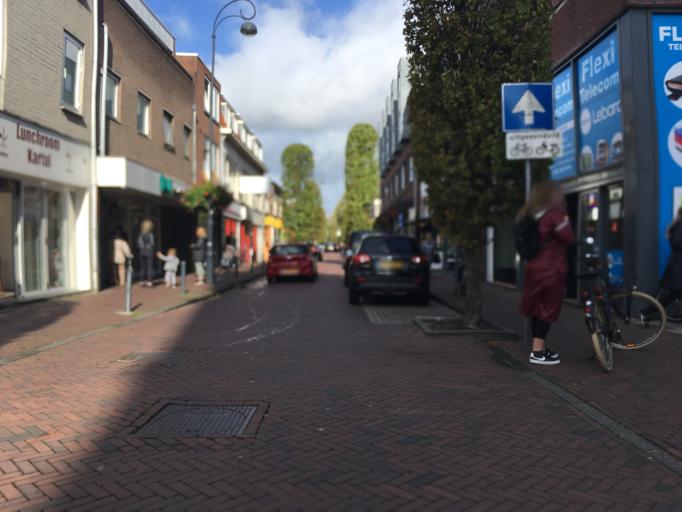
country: NL
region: North Holland
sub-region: Gemeente Haarlem
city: Haarlem
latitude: 52.3787
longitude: 4.6482
